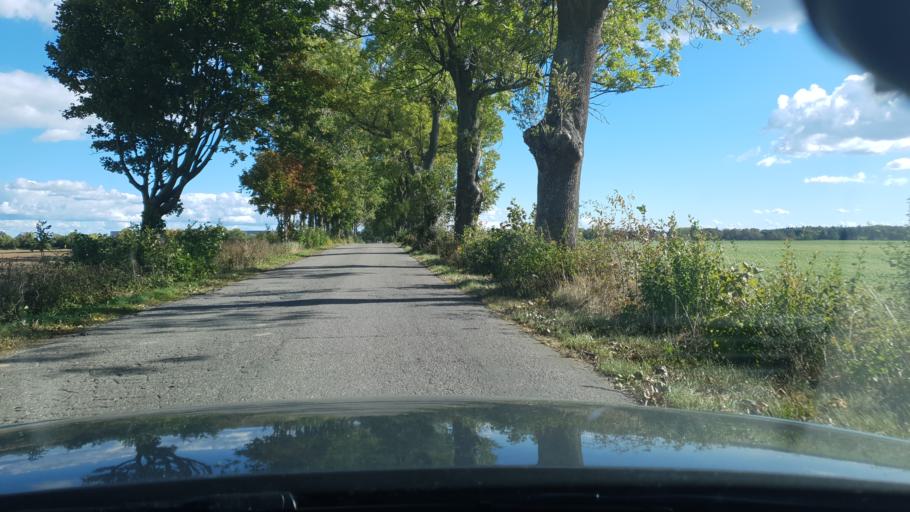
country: PL
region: Pomeranian Voivodeship
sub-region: Powiat pucki
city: Zelistrzewo
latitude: 54.6873
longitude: 18.4438
